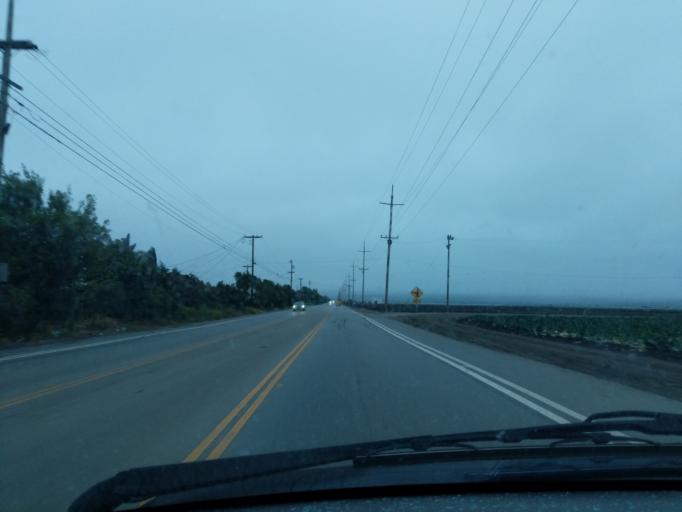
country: US
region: California
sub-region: Monterey County
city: Salinas
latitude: 36.6759
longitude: -121.6773
